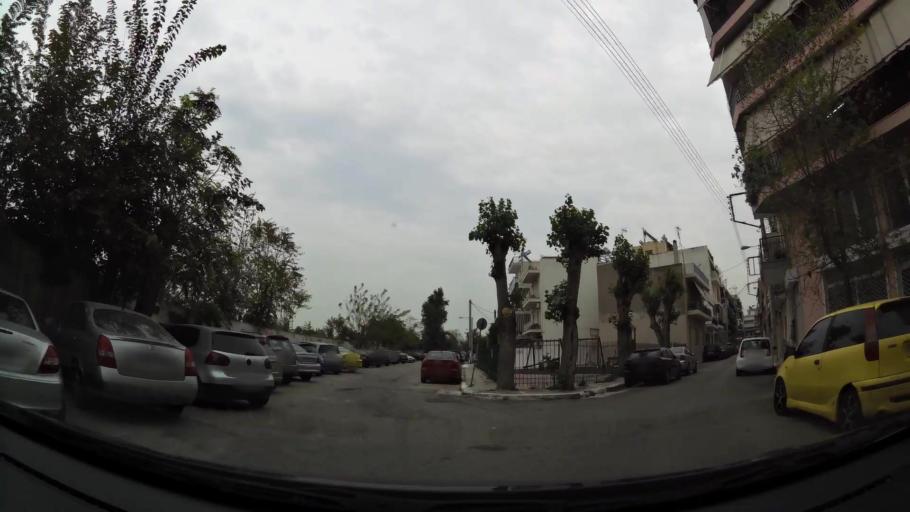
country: GR
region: Attica
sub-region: Nomos Piraios
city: Agios Ioannis Rentis
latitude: 37.9593
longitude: 23.6591
